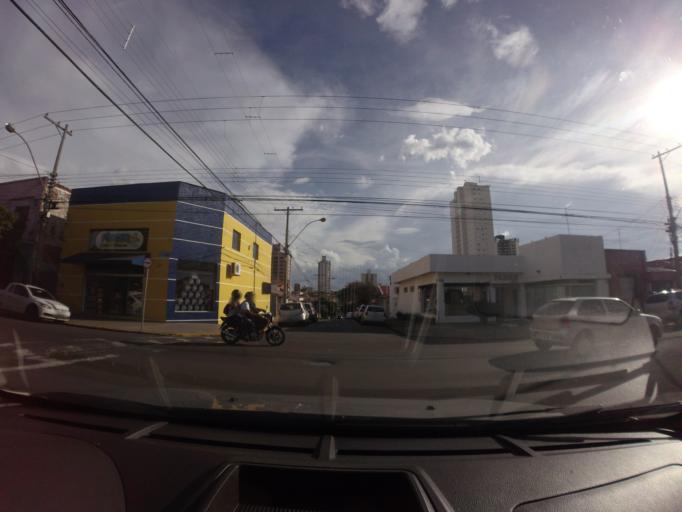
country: BR
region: Sao Paulo
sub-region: Piracicaba
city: Piracicaba
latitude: -22.7244
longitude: -47.6397
